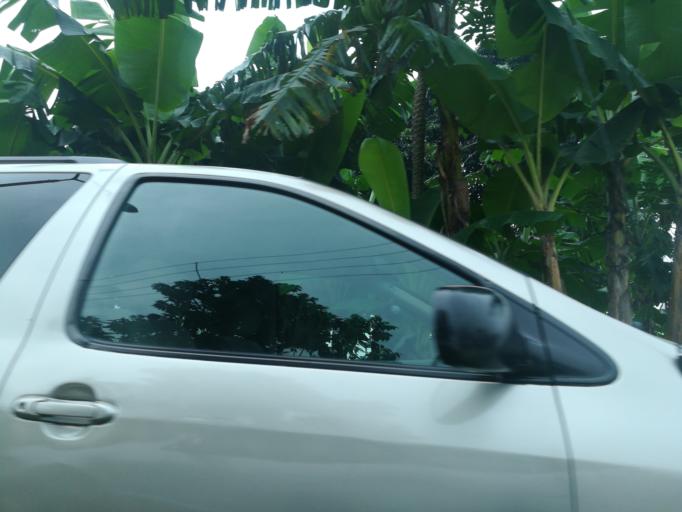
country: NG
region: Rivers
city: Port Harcourt
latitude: 4.7573
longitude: 7.0150
